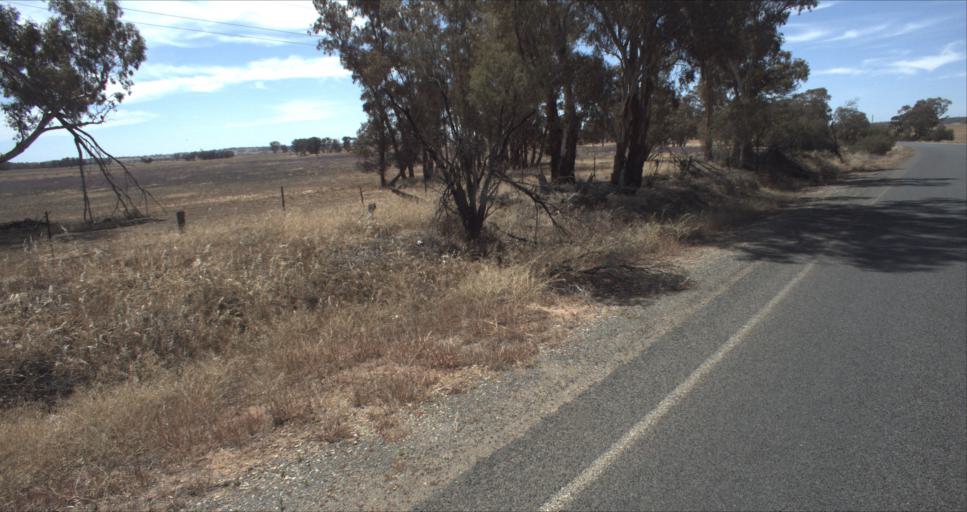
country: AU
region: New South Wales
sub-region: Leeton
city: Leeton
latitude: -34.6600
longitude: 146.4540
